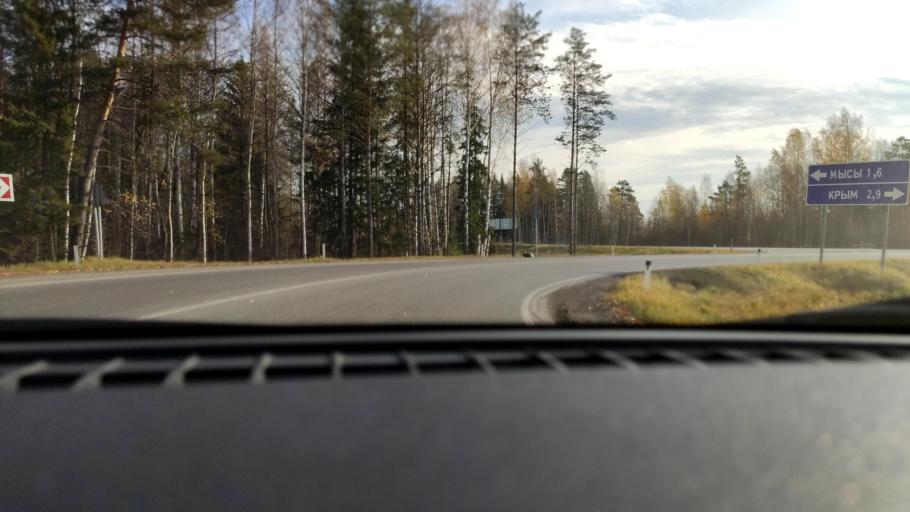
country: RU
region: Perm
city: Overyata
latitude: 58.0458
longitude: 55.8790
